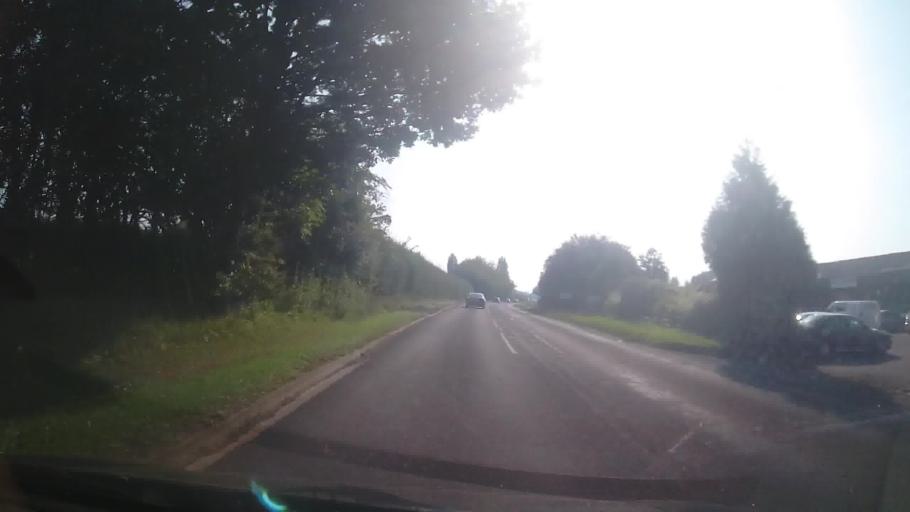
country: GB
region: England
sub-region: Shropshire
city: Much Wenlock
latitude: 52.5579
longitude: -2.5158
